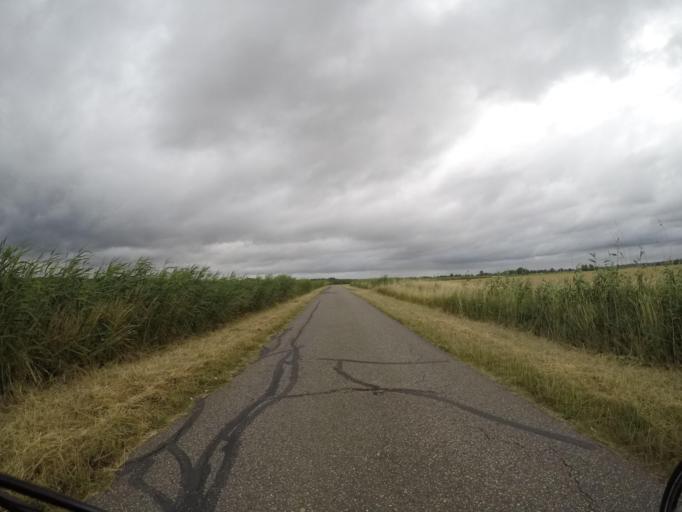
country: DE
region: Lower Saxony
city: Hitzacker
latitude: 53.1658
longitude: 11.0821
